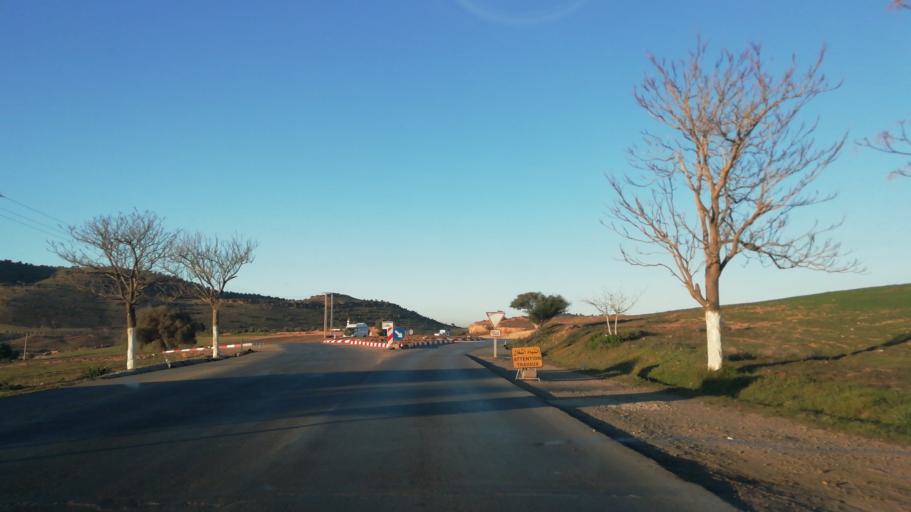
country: DZ
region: Tlemcen
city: Nedroma
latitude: 34.8608
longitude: -1.6787
